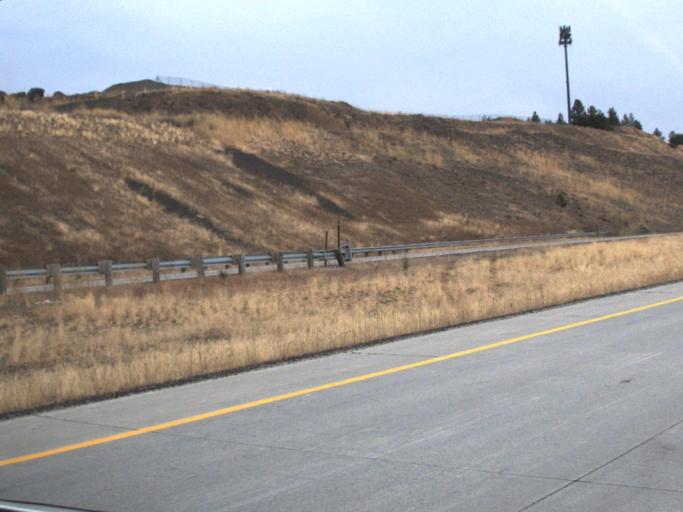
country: US
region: Washington
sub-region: Spokane County
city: Fairwood
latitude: 47.7787
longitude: -117.3886
